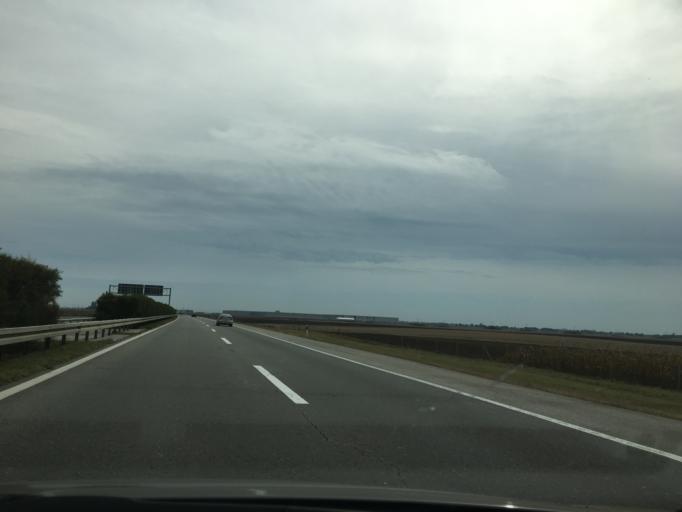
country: RS
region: Autonomna Pokrajina Vojvodina
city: Nova Pazova
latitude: 44.9824
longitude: 20.2192
